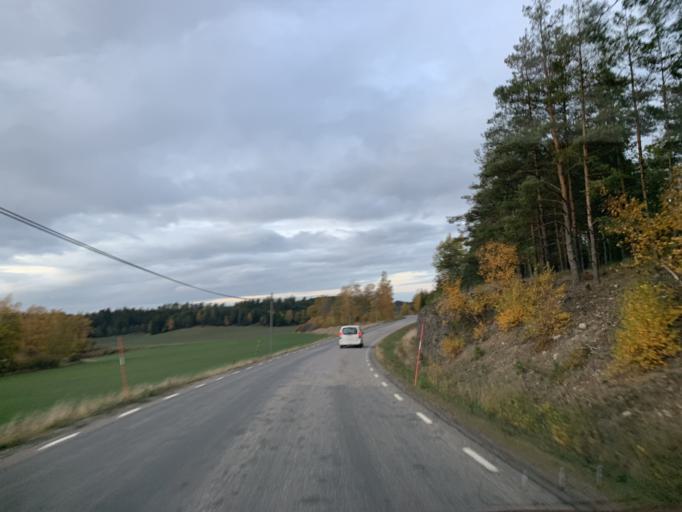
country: SE
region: Stockholm
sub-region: Nynashamns Kommun
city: Osmo
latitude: 58.9444
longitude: 17.7618
